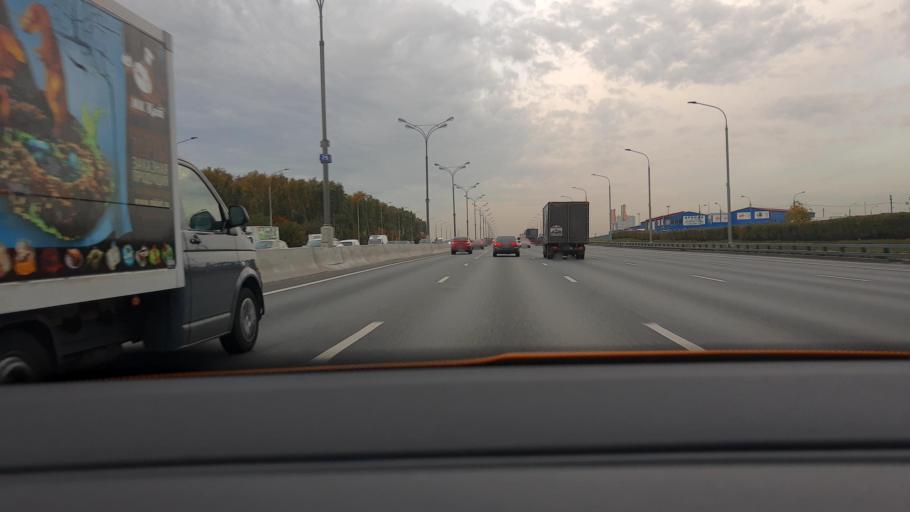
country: RU
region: Moscow
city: Businovo
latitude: 55.8981
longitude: 37.5087
